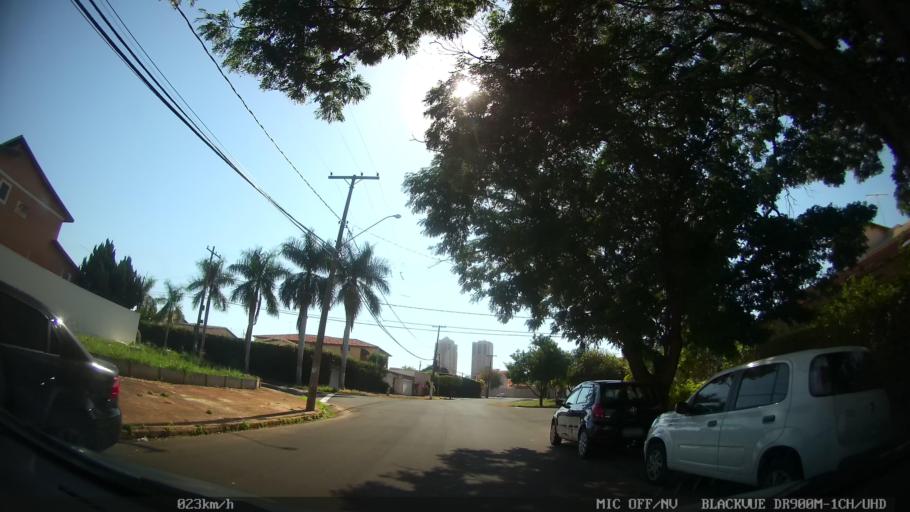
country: BR
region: Sao Paulo
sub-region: Ribeirao Preto
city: Ribeirao Preto
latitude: -21.2047
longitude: -47.7724
